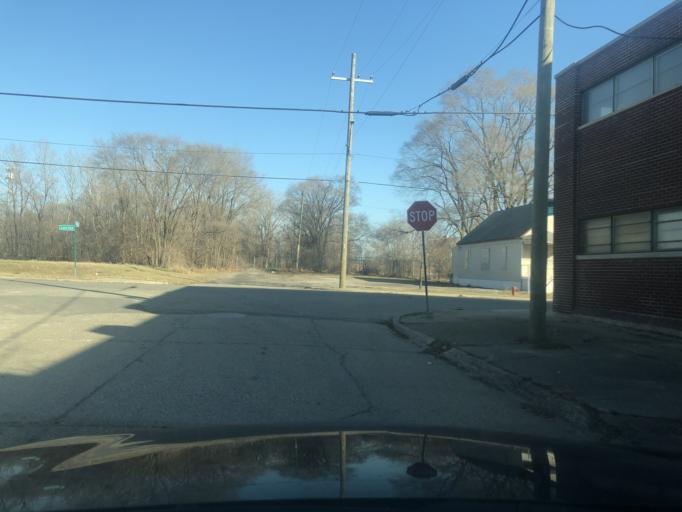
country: US
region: Michigan
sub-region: Wayne County
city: River Rouge
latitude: 42.3062
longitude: -83.0938
